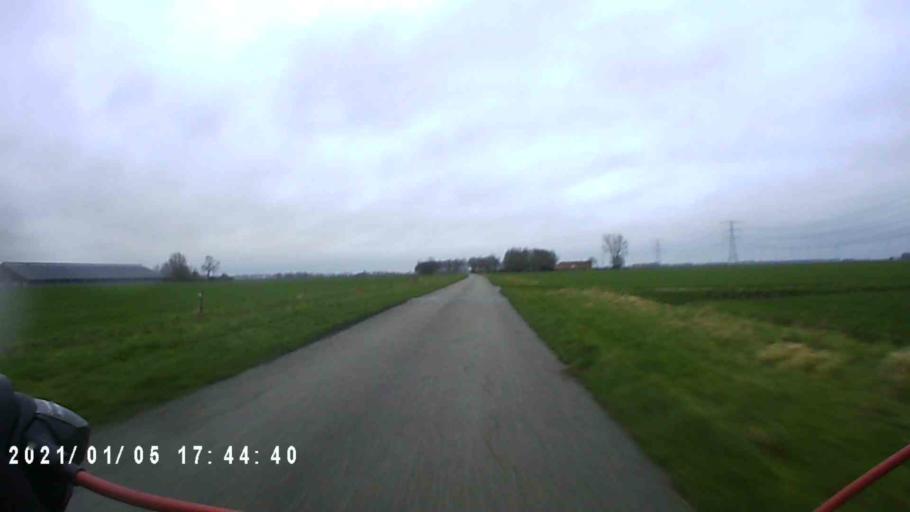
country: NL
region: Groningen
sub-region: Gemeente Slochteren
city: Slochteren
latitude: 53.2106
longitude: 6.9104
